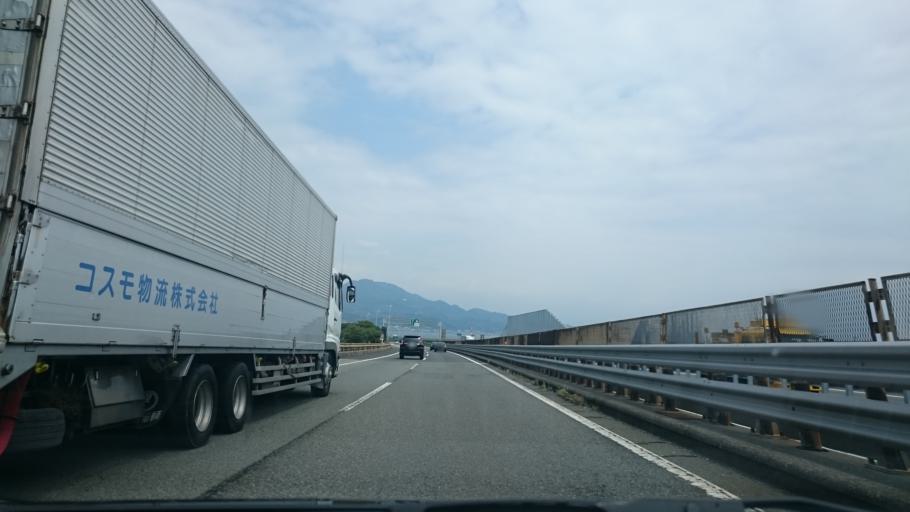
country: JP
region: Shizuoka
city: Fujinomiya
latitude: 35.0740
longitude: 138.5443
